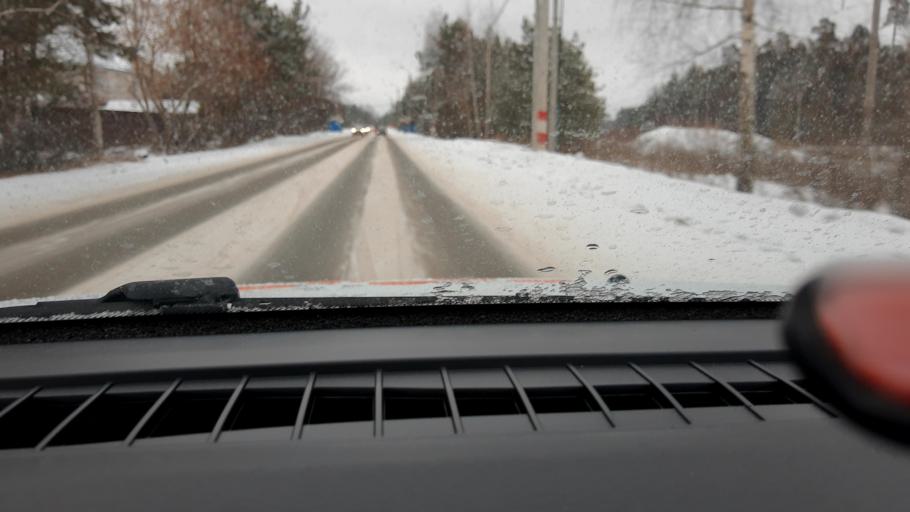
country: RU
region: Nizjnij Novgorod
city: Bor
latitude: 56.3265
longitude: 44.1330
